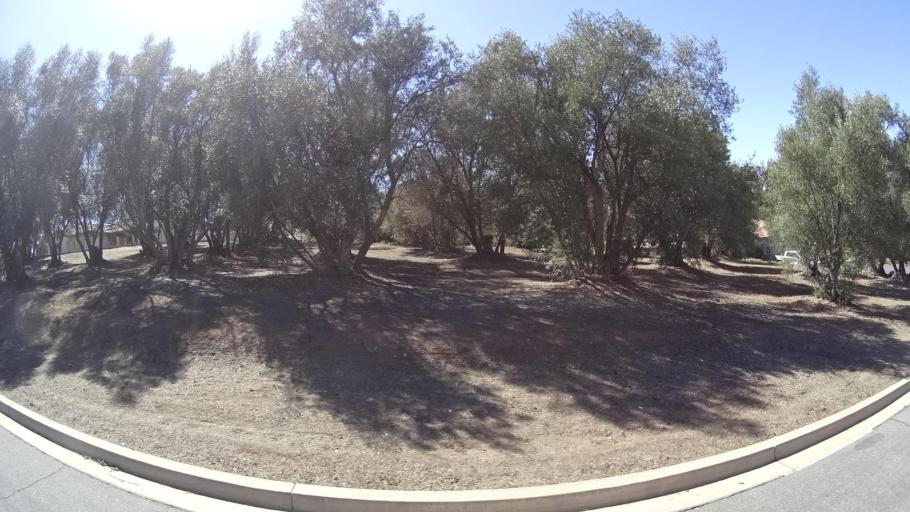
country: US
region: California
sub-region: San Diego County
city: Alpine
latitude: 32.8095
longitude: -116.7786
